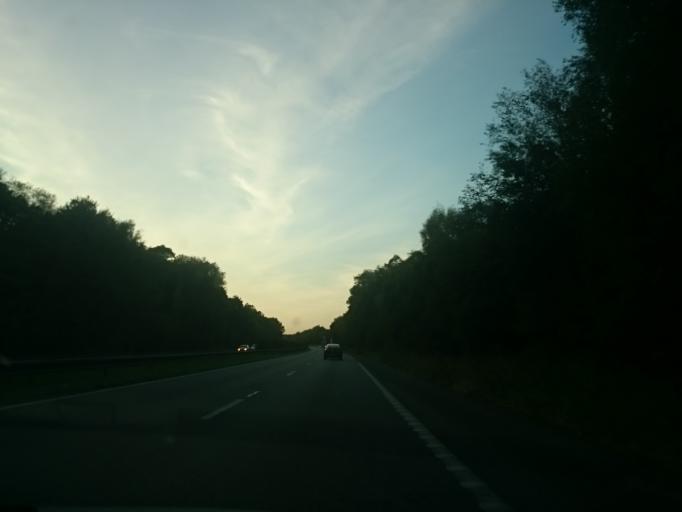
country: FR
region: Brittany
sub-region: Departement du Morbihan
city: Gestel
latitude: 47.8168
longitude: -3.4639
